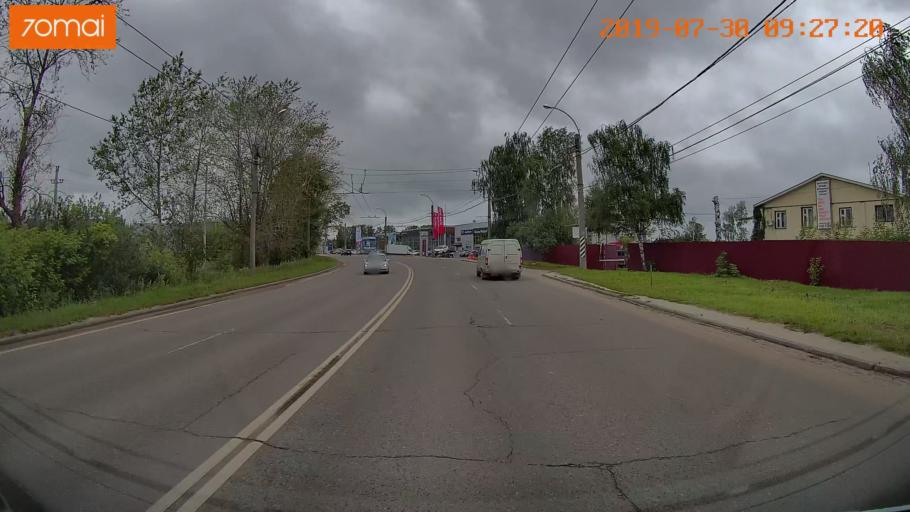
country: RU
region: Ivanovo
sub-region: Gorod Ivanovo
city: Ivanovo
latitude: 56.9469
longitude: 40.9706
